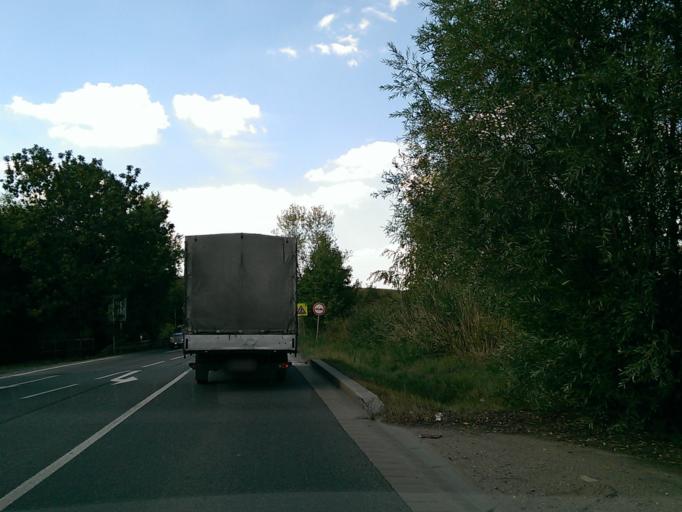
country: CZ
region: Praha
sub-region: Praha 14
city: Hostavice
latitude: 50.0631
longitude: 14.5535
